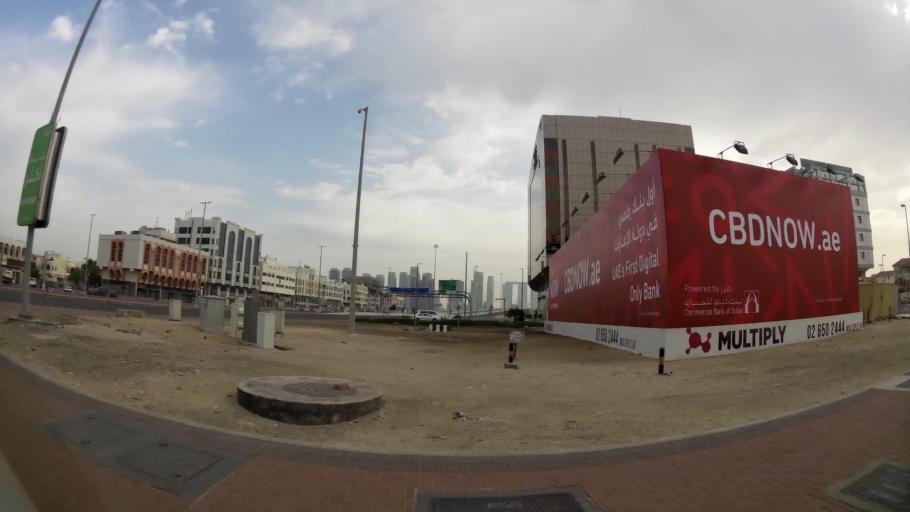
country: AE
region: Abu Dhabi
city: Abu Dhabi
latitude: 24.4777
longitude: 54.3820
